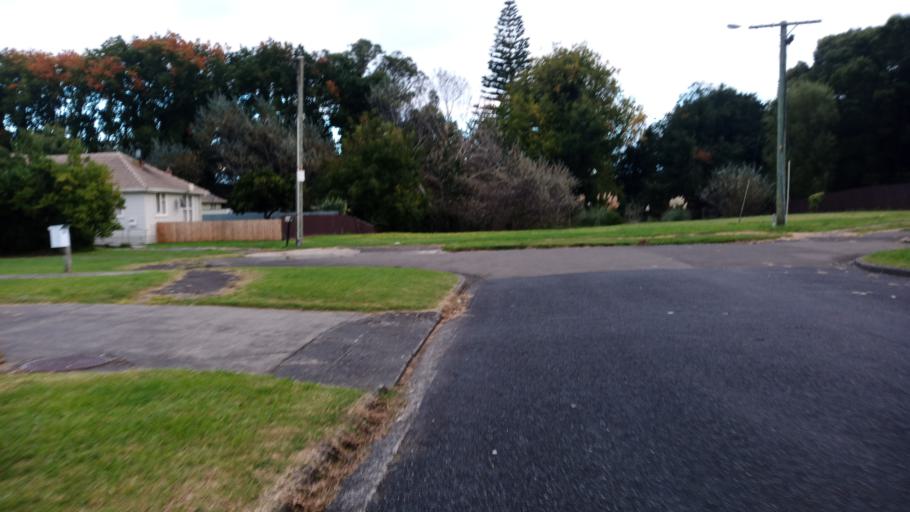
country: NZ
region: Gisborne
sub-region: Gisborne District
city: Gisborne
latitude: -38.6571
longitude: 178.0002
